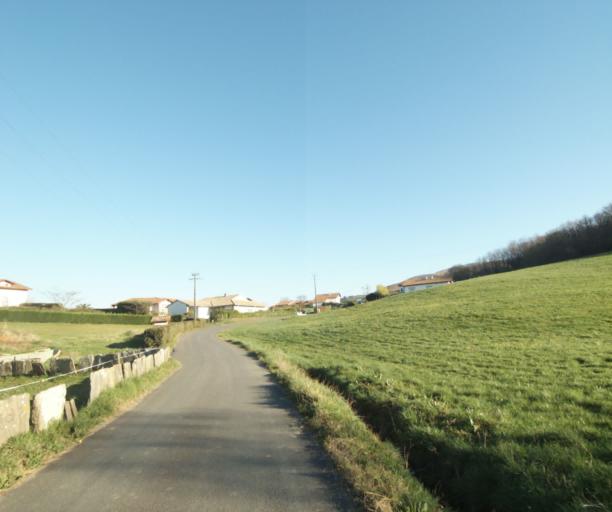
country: FR
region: Aquitaine
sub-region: Departement des Pyrenees-Atlantiques
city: Urrugne
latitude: 43.3516
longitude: -1.7230
